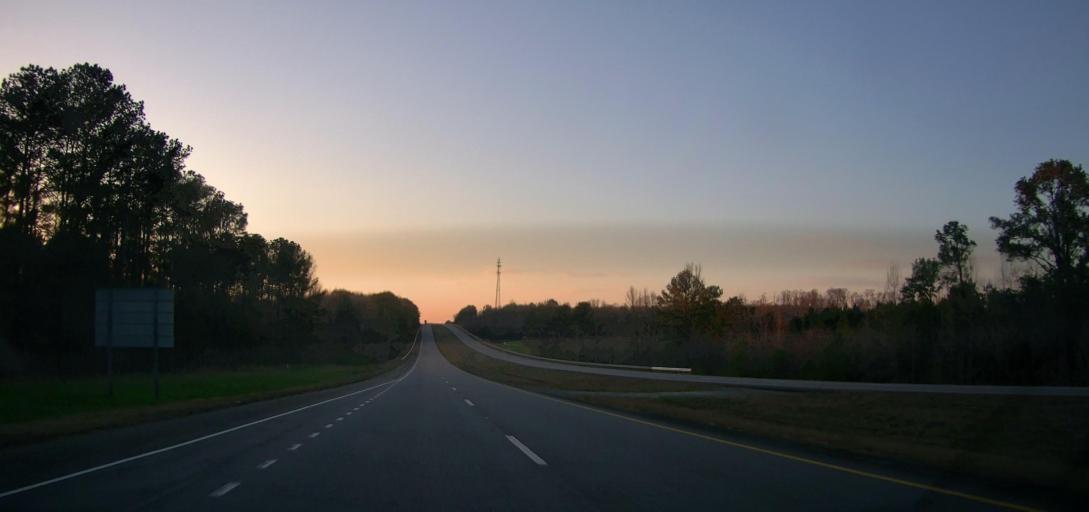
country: US
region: Alabama
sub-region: Coosa County
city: Goodwater
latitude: 32.9898
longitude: -86.0707
